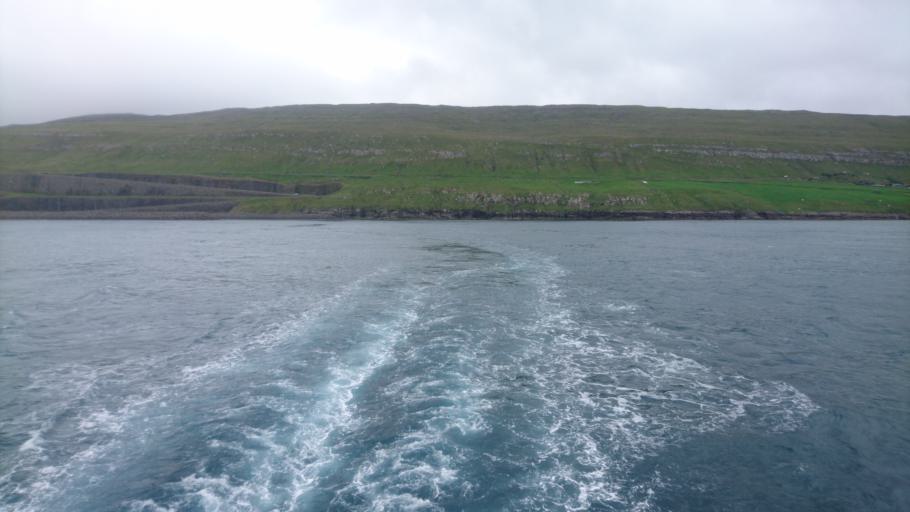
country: FO
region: Streymoy
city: Argir
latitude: 61.9546
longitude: -6.8222
